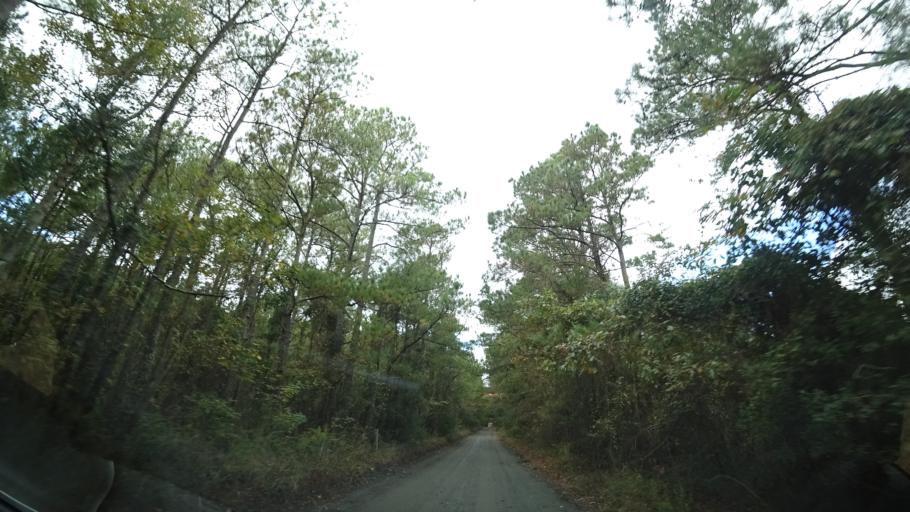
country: US
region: North Carolina
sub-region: Dare County
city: Kill Devil Hills
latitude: 35.9986
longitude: -75.6633
